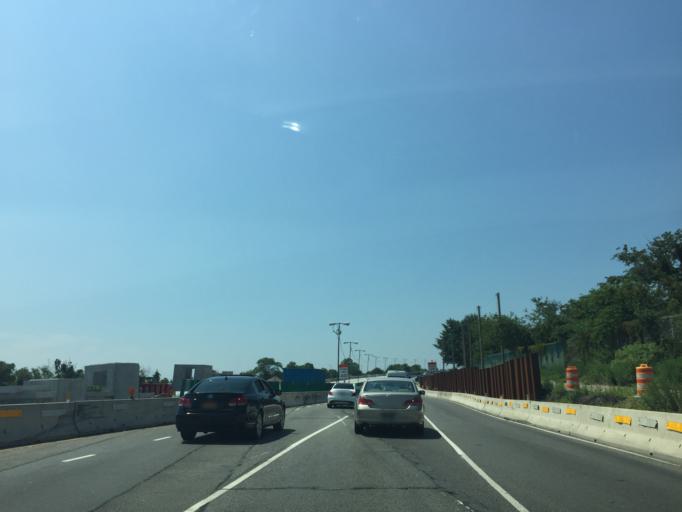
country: US
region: New York
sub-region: Kings County
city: Brooklyn
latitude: 40.5907
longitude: -73.9084
